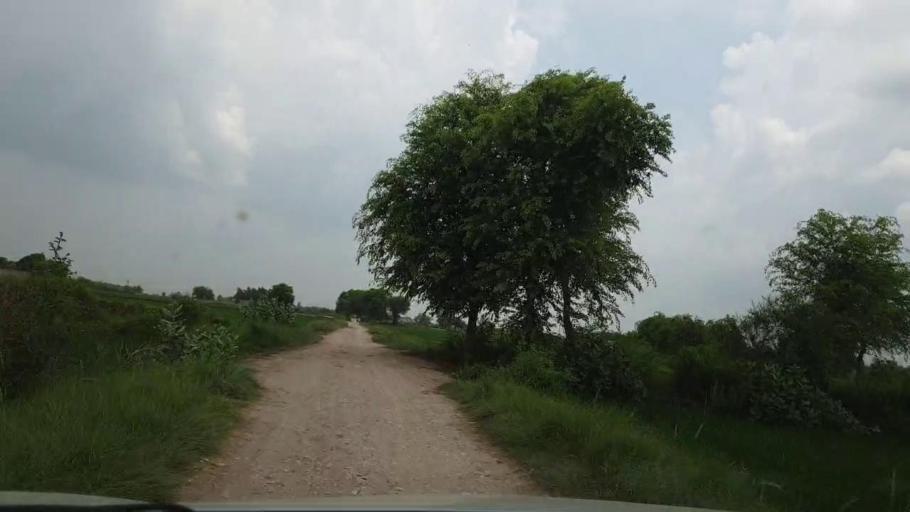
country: PK
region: Sindh
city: Goth Garelo
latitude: 27.4303
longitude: 68.0855
